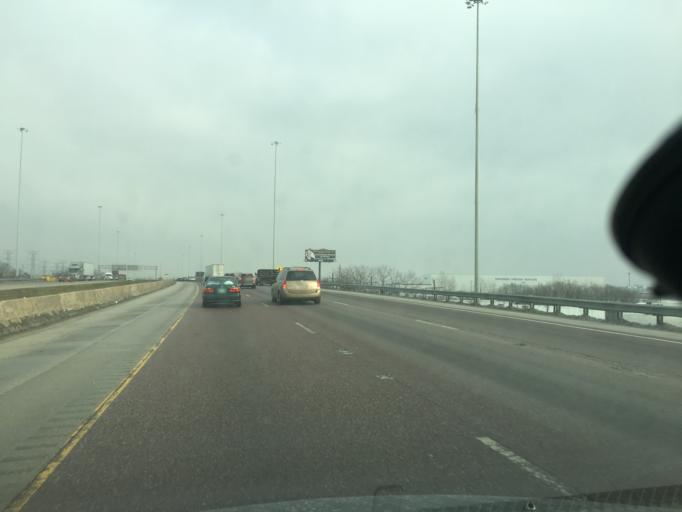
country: US
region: Illinois
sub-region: Cook County
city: Cicero
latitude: 41.8177
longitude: -87.7415
